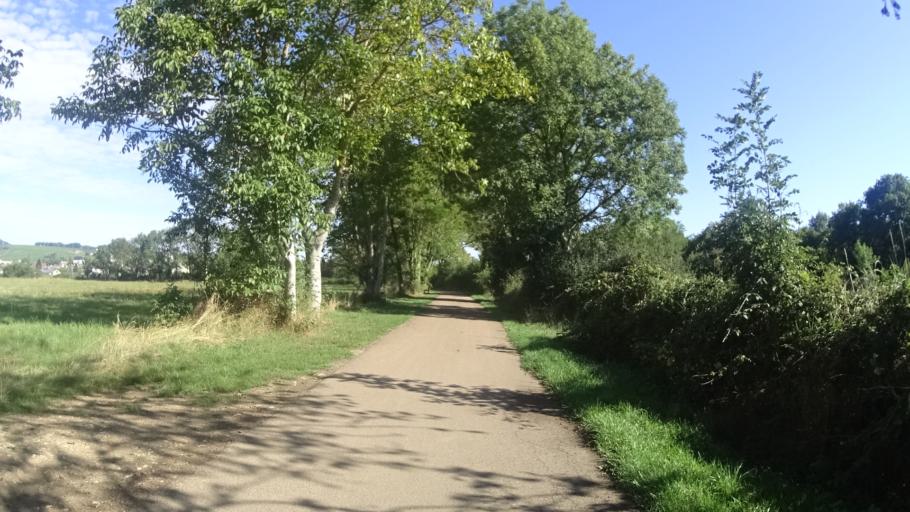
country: FR
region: Centre
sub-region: Departement du Cher
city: Saint-Satur
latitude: 47.3311
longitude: 2.8631
